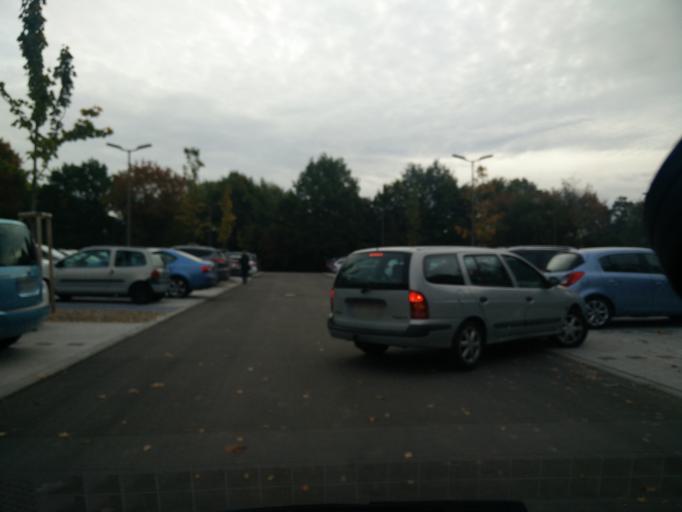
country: DE
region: Baden-Wuerttemberg
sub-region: Karlsruhe Region
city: Ettlingen
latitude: 48.9315
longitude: 8.4749
